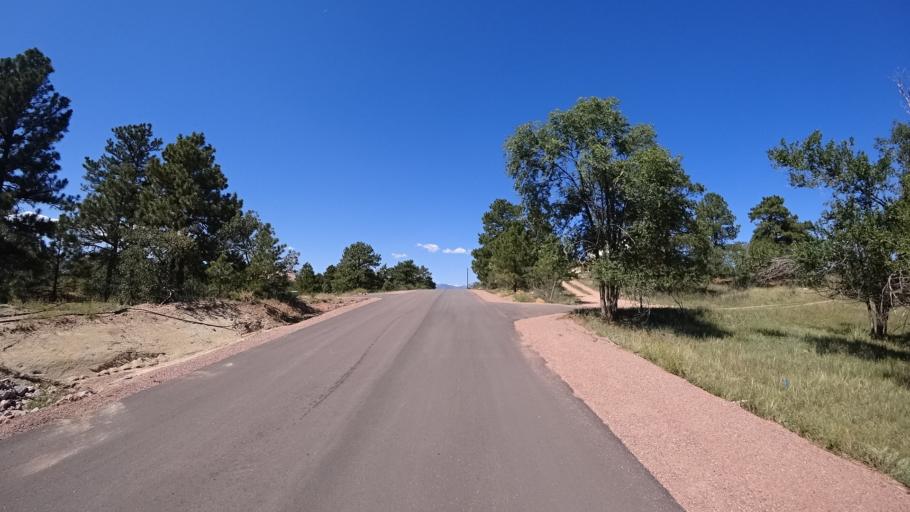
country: US
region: Colorado
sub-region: El Paso County
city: Cimarron Hills
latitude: 38.8629
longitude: -104.7396
